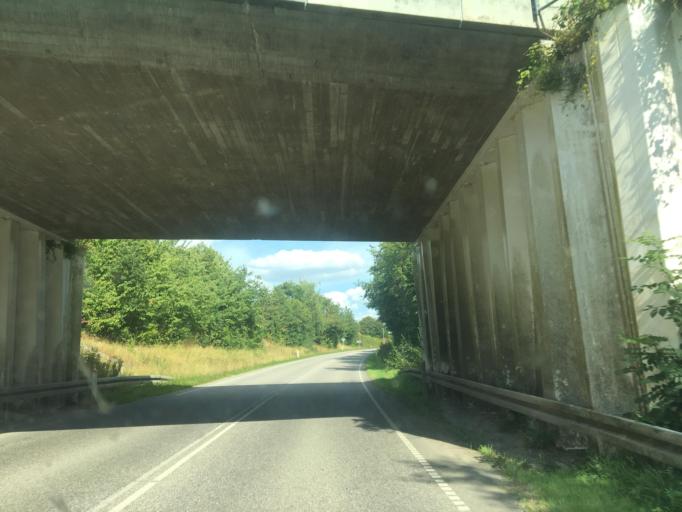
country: DK
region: South Denmark
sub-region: Middelfart Kommune
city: Ejby
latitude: 55.4001
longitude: 9.9689
